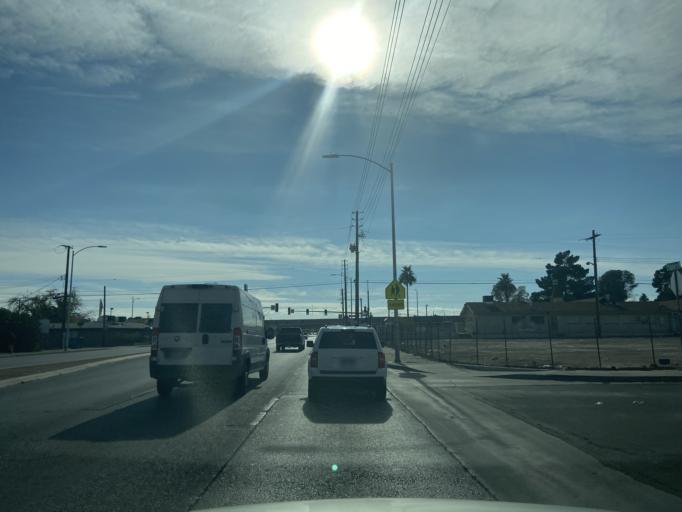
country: US
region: Nevada
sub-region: Clark County
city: Las Vegas
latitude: 36.1713
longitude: -115.1161
